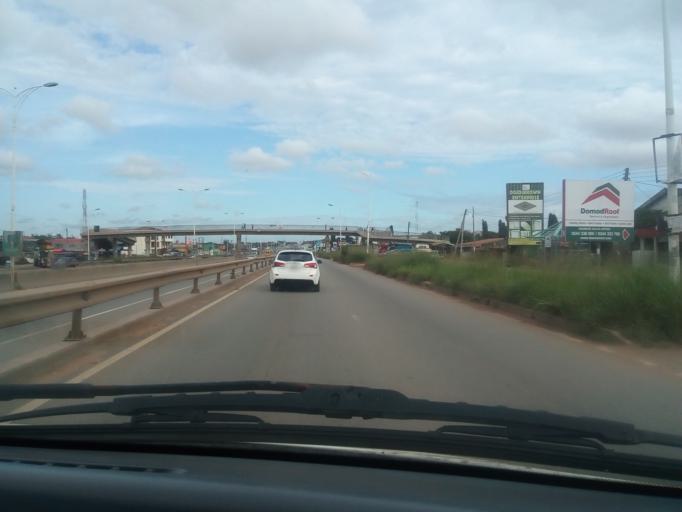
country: GH
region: Greater Accra
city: Dome
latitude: 5.6542
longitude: -0.2605
